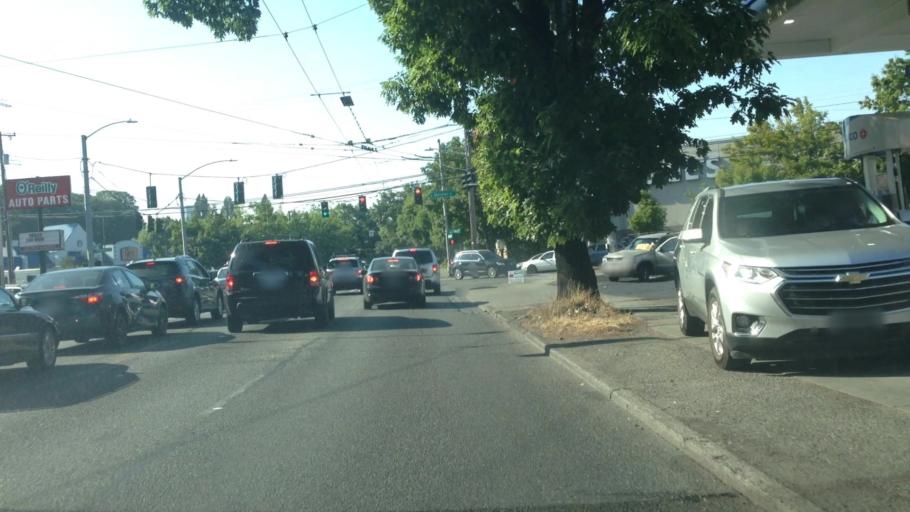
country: US
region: Washington
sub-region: King County
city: Seattle
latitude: 47.5779
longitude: -122.2977
